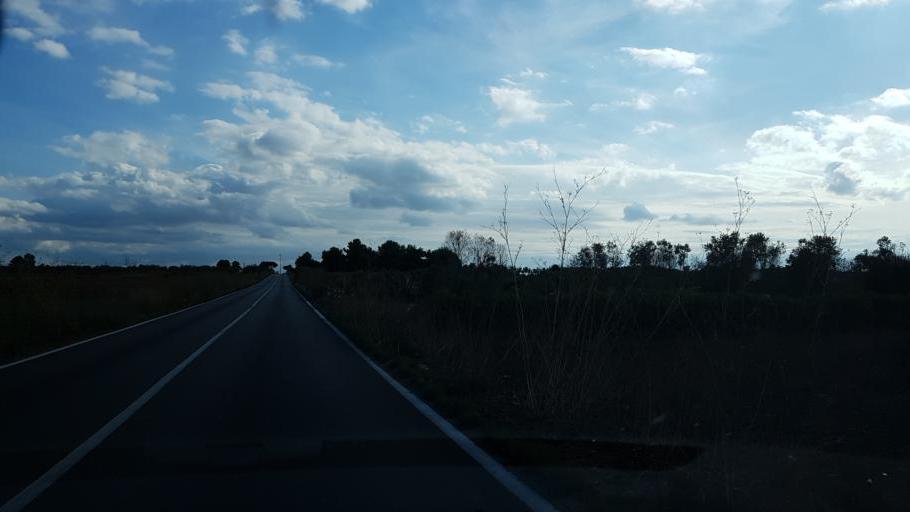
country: IT
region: Apulia
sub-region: Provincia di Lecce
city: Nardo
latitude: 40.1357
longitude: 18.0191
